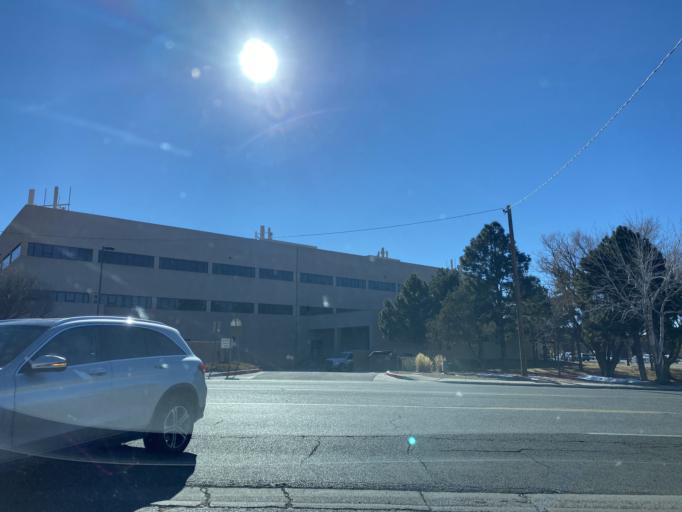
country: US
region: New Mexico
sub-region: Santa Fe County
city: Santa Fe
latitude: 35.6745
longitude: -105.9546
